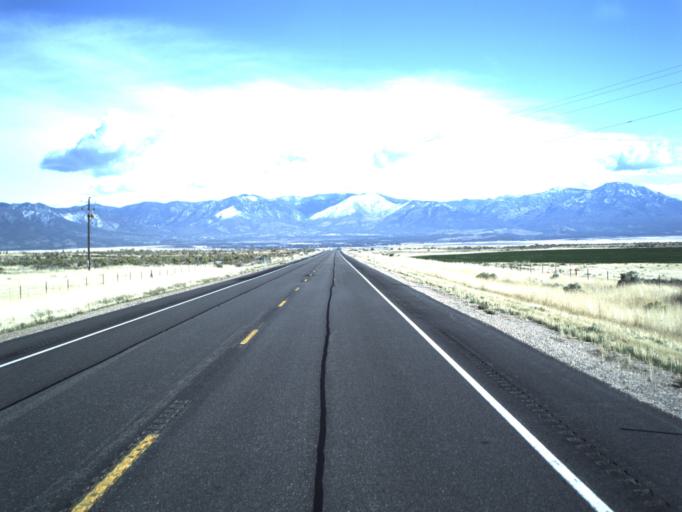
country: US
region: Utah
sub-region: Millard County
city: Fillmore
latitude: 39.1396
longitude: -112.3728
